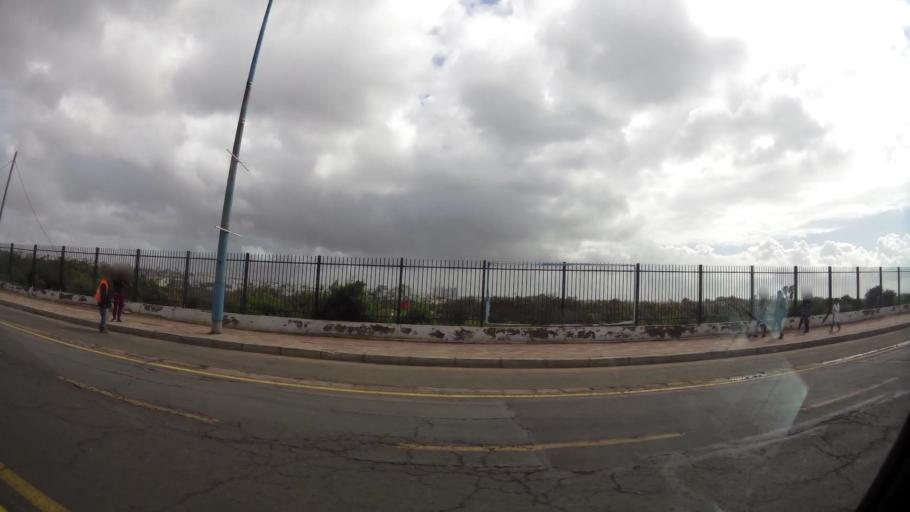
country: MA
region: Grand Casablanca
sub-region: Casablanca
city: Casablanca
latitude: 33.5824
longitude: -7.6974
